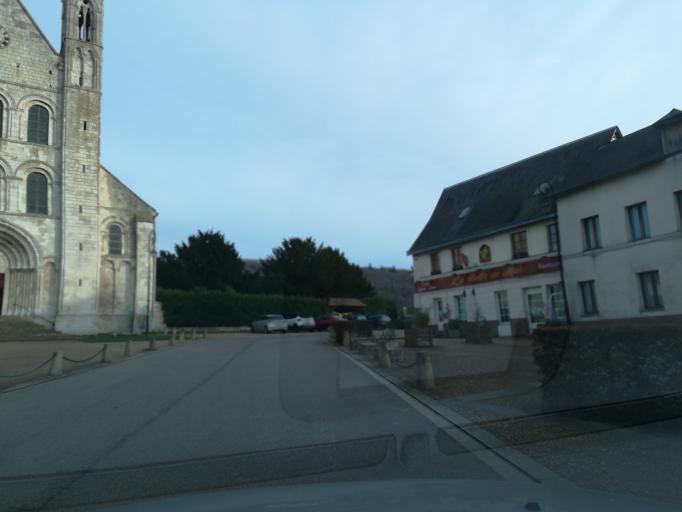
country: FR
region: Haute-Normandie
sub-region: Departement de la Seine-Maritime
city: Saint-Martin-de-Boscherville
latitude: 49.4445
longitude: 0.9634
